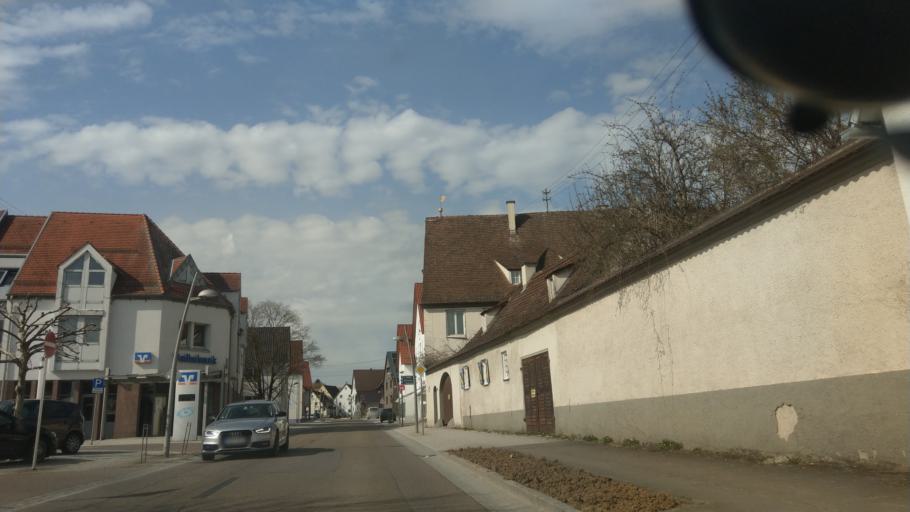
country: DE
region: Baden-Wuerttemberg
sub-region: Regierungsbezirk Stuttgart
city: Niederstotzingen
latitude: 48.5391
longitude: 10.2362
